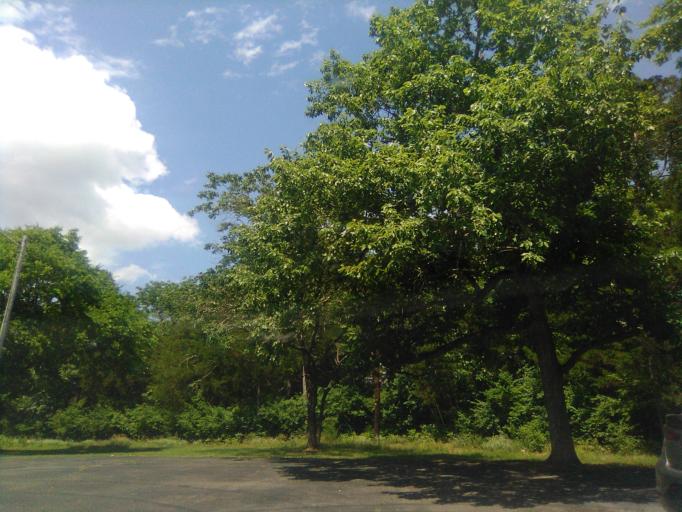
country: US
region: Tennessee
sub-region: Davidson County
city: Belle Meade
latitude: 36.1174
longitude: -86.8777
